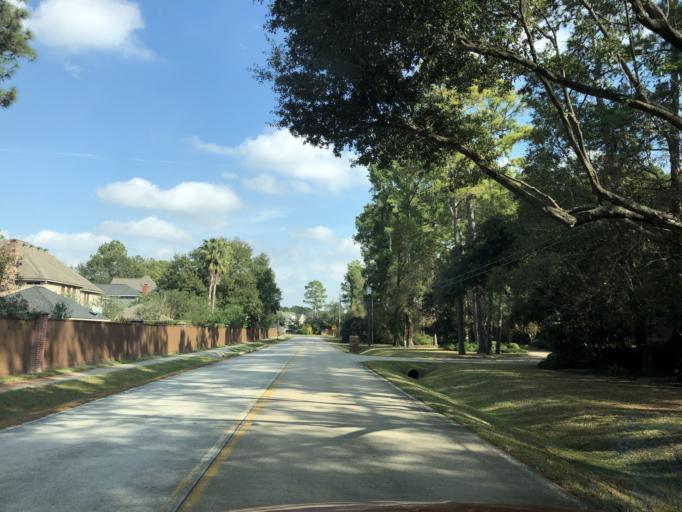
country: US
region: Texas
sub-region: Harris County
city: Tomball
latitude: 30.0285
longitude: -95.5461
